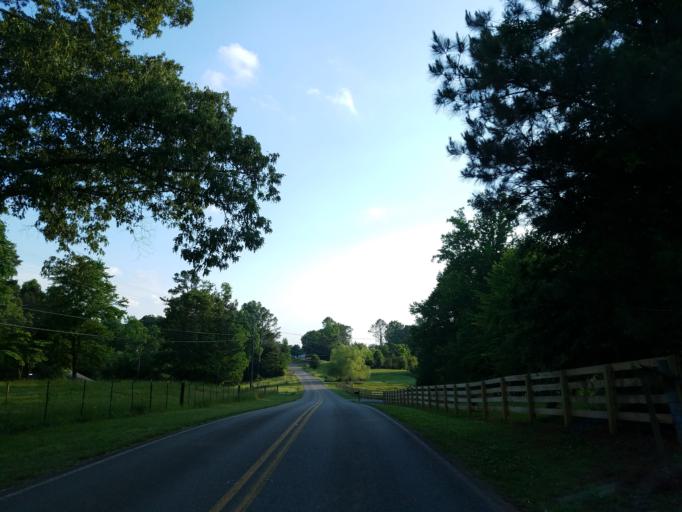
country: US
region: Georgia
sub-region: Cherokee County
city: Ball Ground
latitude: 34.3247
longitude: -84.3685
